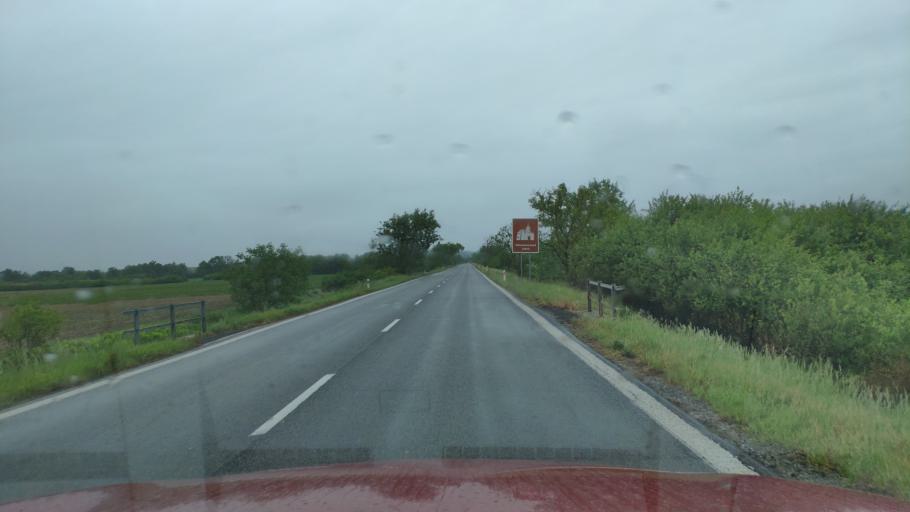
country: HU
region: Borsod-Abauj-Zemplen
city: Karcsa
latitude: 48.4346
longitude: 21.8724
